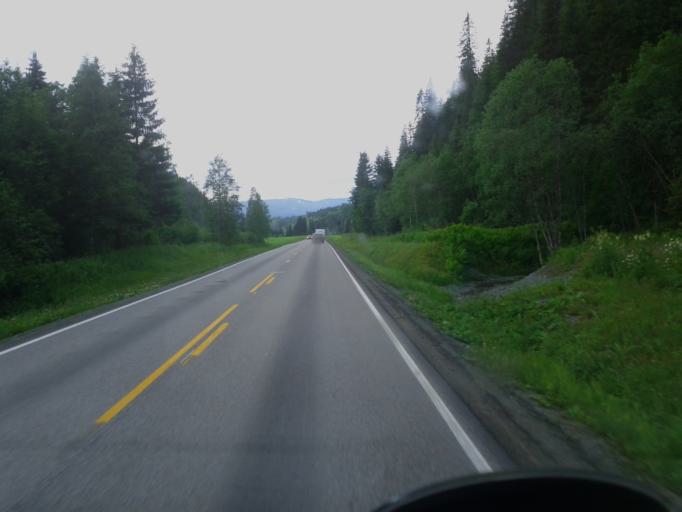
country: NO
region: Nord-Trondelag
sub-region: Grong
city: Grong
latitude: 64.5163
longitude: 12.3746
